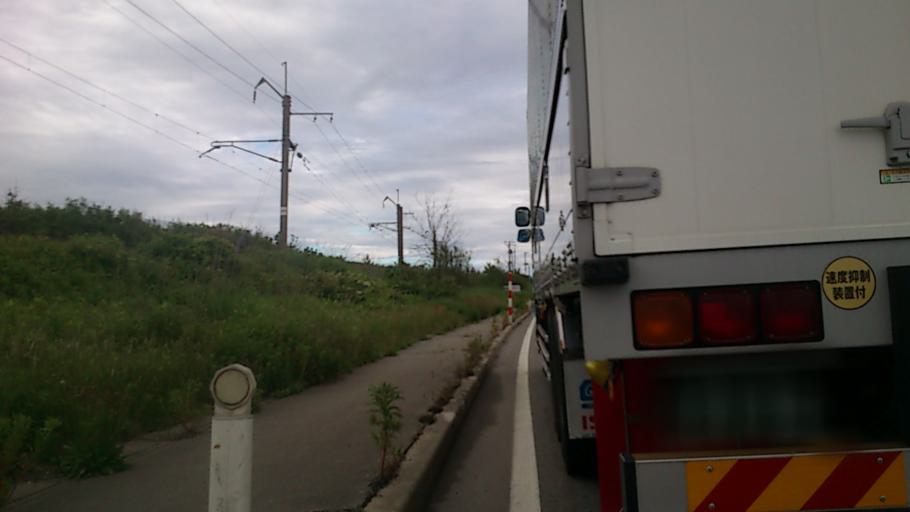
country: JP
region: Akita
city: Akita Shi
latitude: 39.6380
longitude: 140.0656
